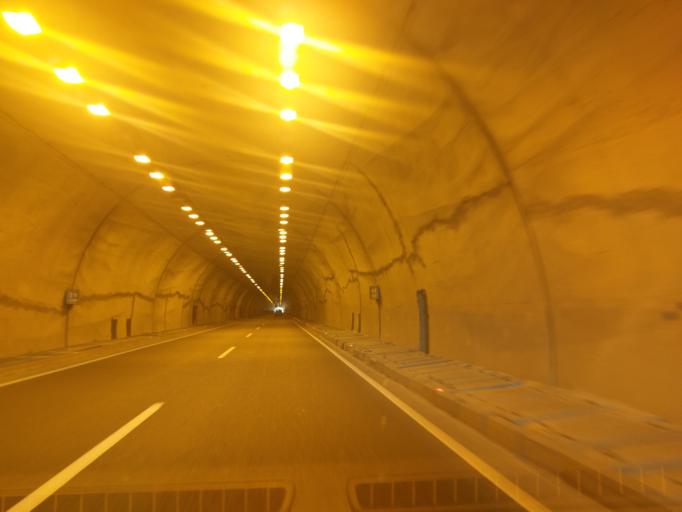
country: TR
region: Ordu
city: Unieh
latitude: 41.1140
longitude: 37.2869
